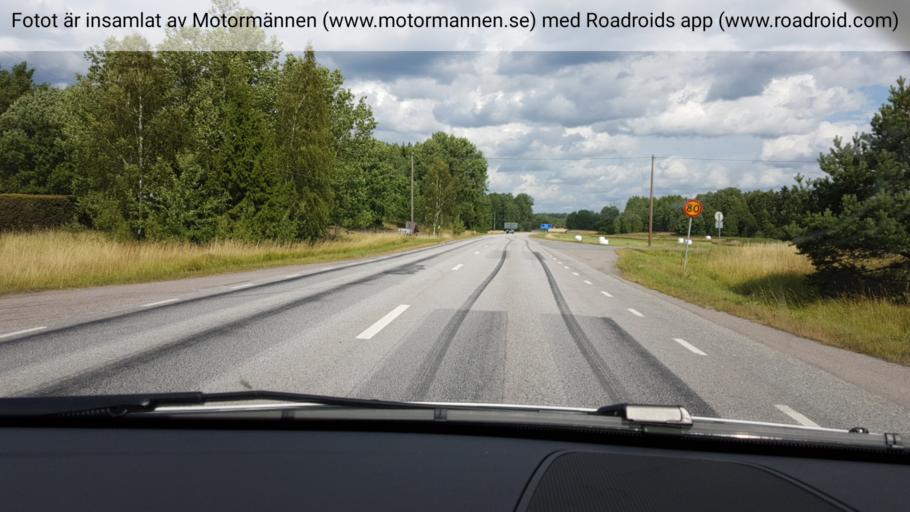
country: SE
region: Stockholm
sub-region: Vallentuna Kommun
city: Vallentuna
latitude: 59.7531
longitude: 18.0433
